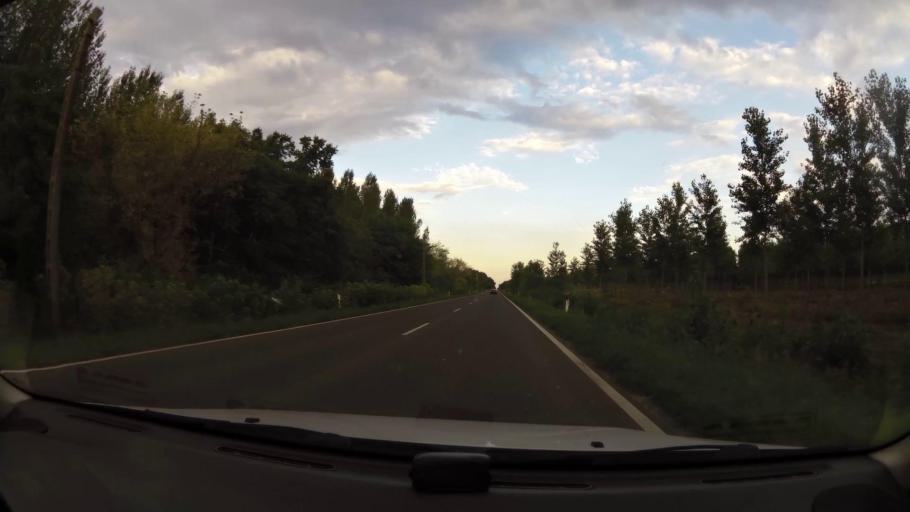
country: HU
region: Pest
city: Tapioszele
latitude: 47.3014
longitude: 19.8888
